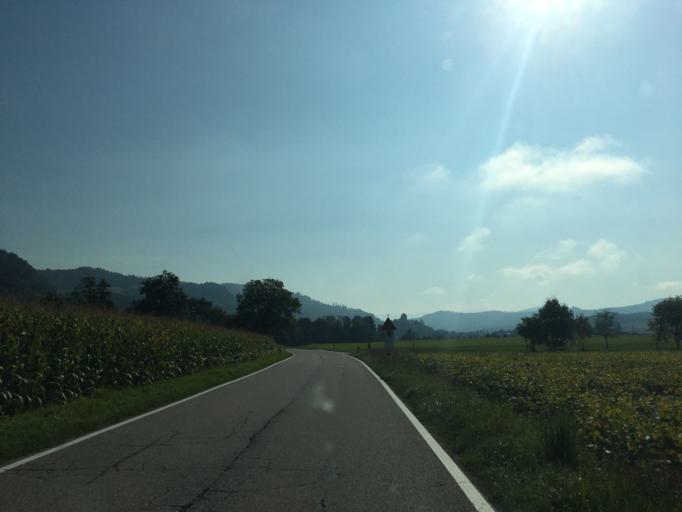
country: AT
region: Carinthia
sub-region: Politischer Bezirk Volkermarkt
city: Voelkermarkt
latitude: 46.6930
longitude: 14.6472
